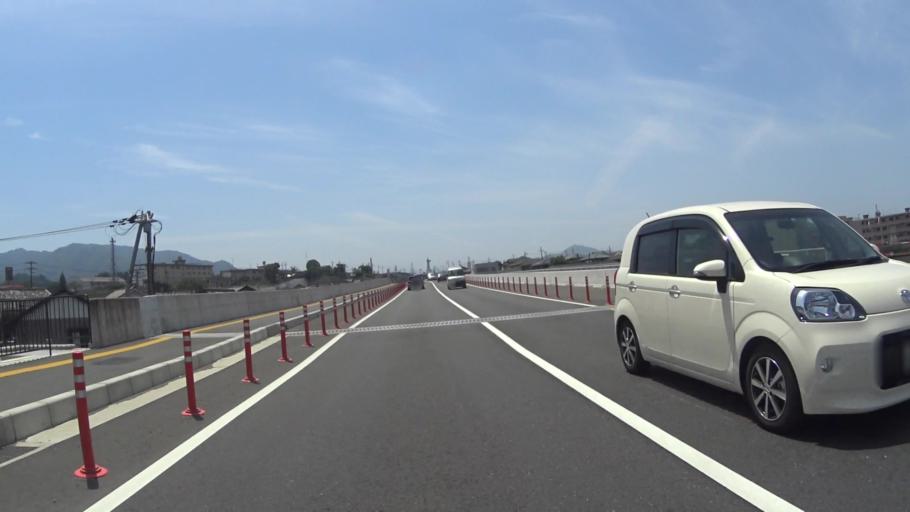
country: JP
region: Kyoto
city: Fukuchiyama
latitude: 35.2908
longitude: 135.1302
